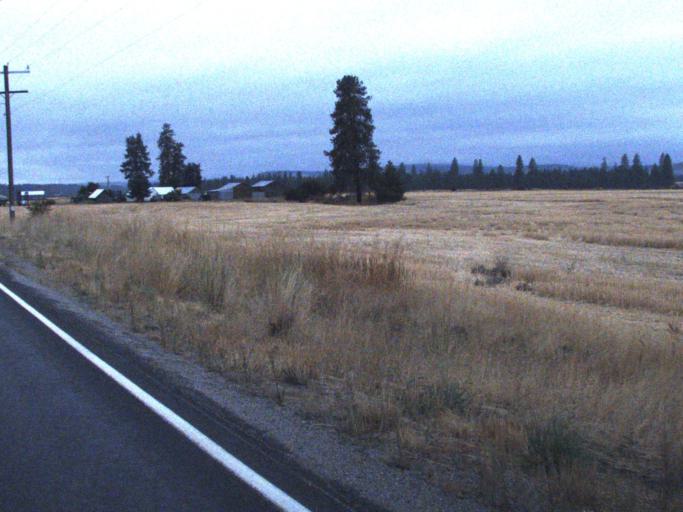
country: US
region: Washington
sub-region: Spokane County
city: Deer Park
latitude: 47.9440
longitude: -117.7659
